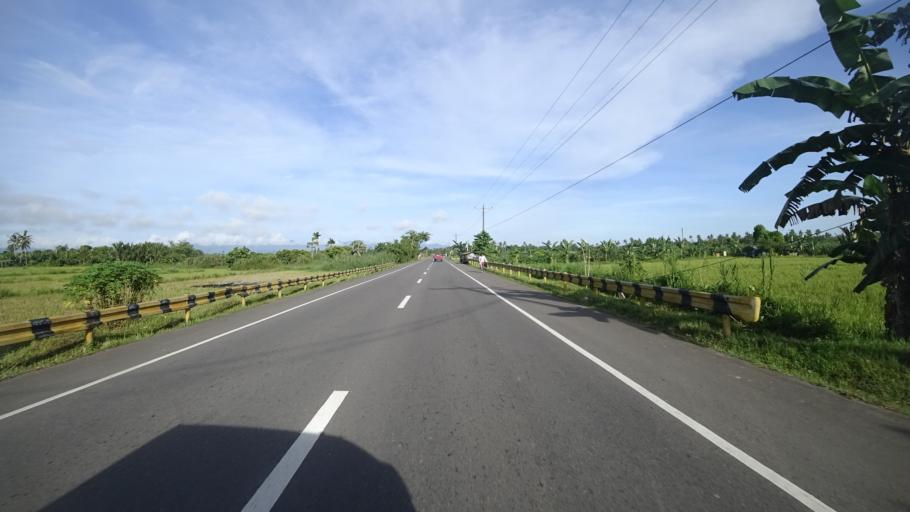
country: PH
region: Eastern Visayas
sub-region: Province of Leyte
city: Santa Fe
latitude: 11.1922
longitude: 124.8856
